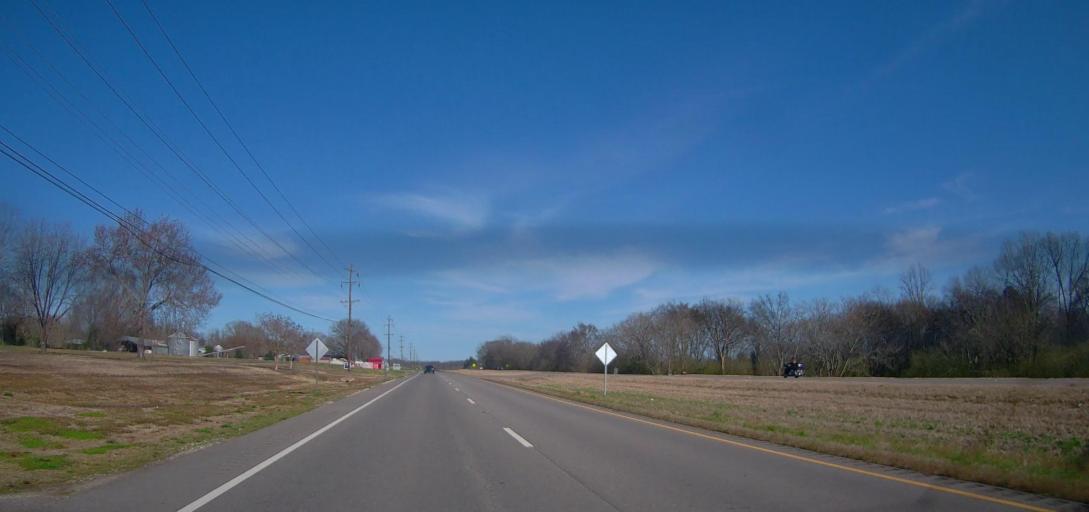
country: US
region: Alabama
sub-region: Lauderdale County
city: Killen
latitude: 34.8600
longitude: -87.4300
